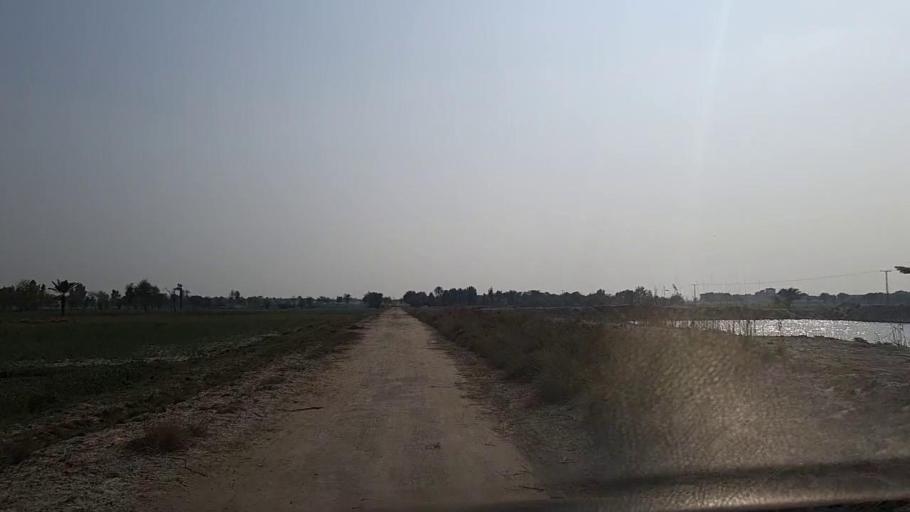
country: PK
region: Sindh
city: Daur
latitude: 26.4033
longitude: 68.4201
